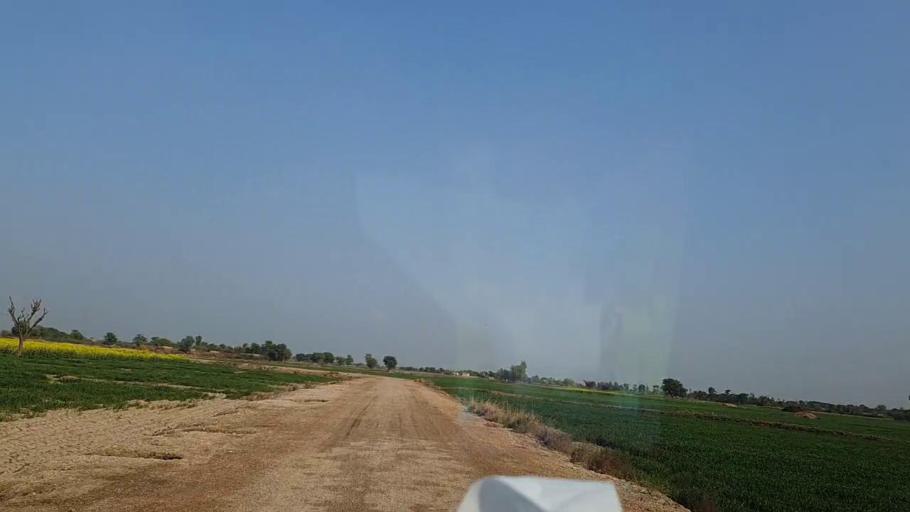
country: PK
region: Sindh
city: Nawabshah
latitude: 26.1588
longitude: 68.4104
